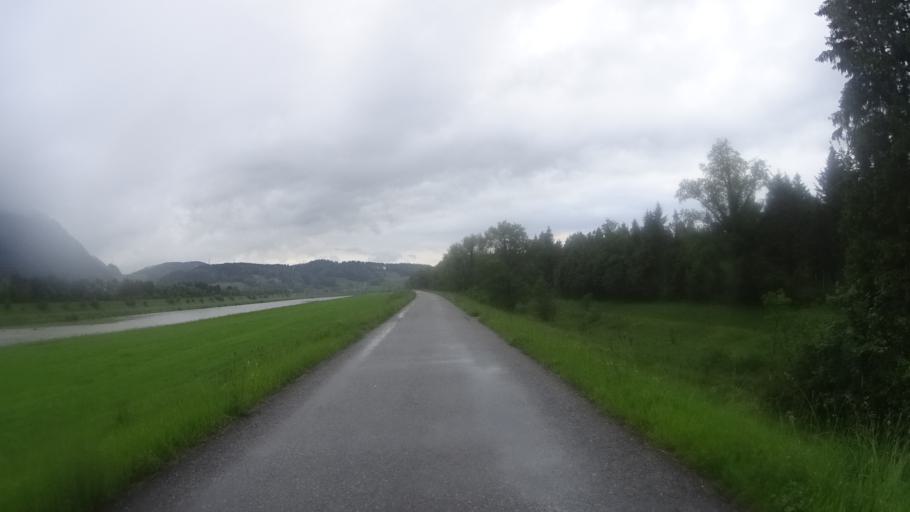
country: CH
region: Saint Gallen
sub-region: Wahlkreis Rheintal
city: Ruthi
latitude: 47.2874
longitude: 9.5534
